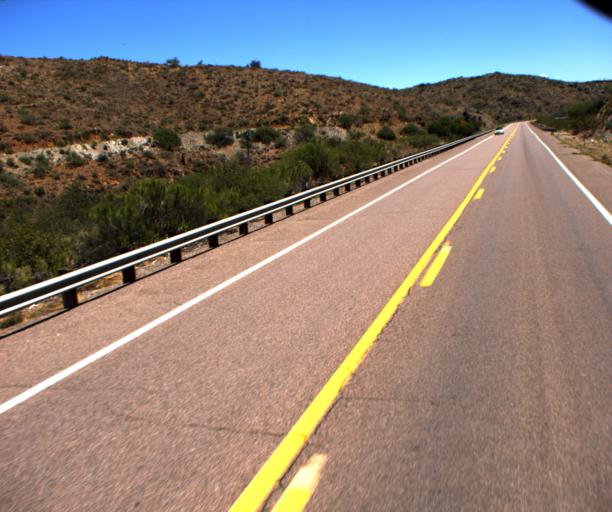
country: US
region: Arizona
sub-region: Yavapai County
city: Bagdad
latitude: 34.5572
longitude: -113.1602
